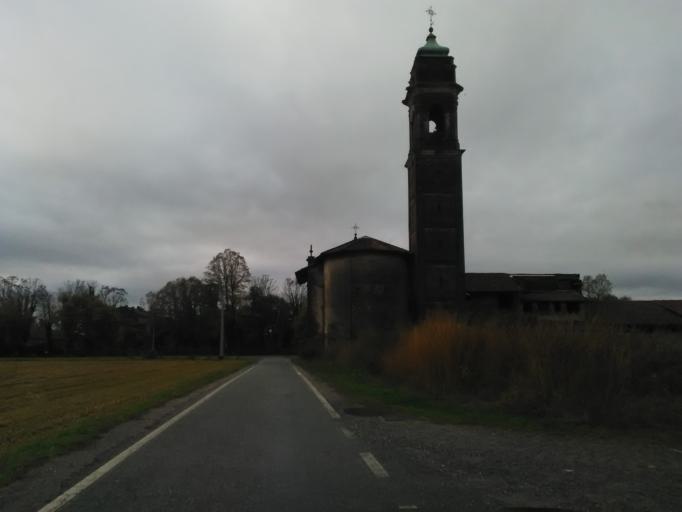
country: IT
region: Piedmont
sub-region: Provincia di Vercelli
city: Carisio
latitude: 45.3952
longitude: 8.2387
